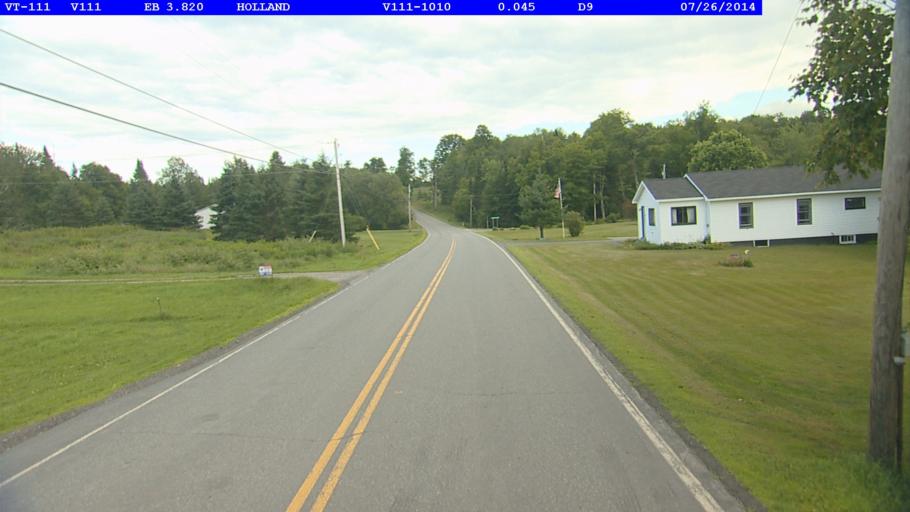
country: US
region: Vermont
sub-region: Orleans County
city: Newport
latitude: 44.9319
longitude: -72.0650
